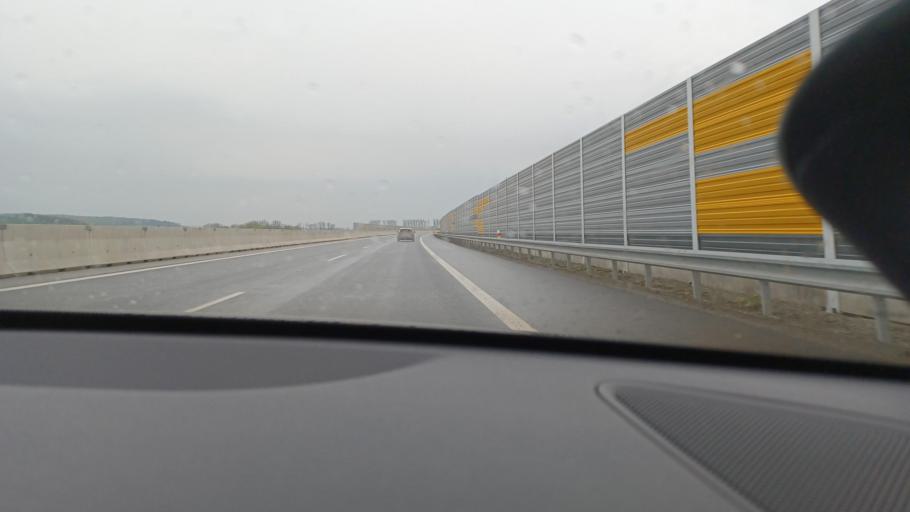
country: SK
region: Kosicky
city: Kosice
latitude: 48.7620
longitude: 21.3271
